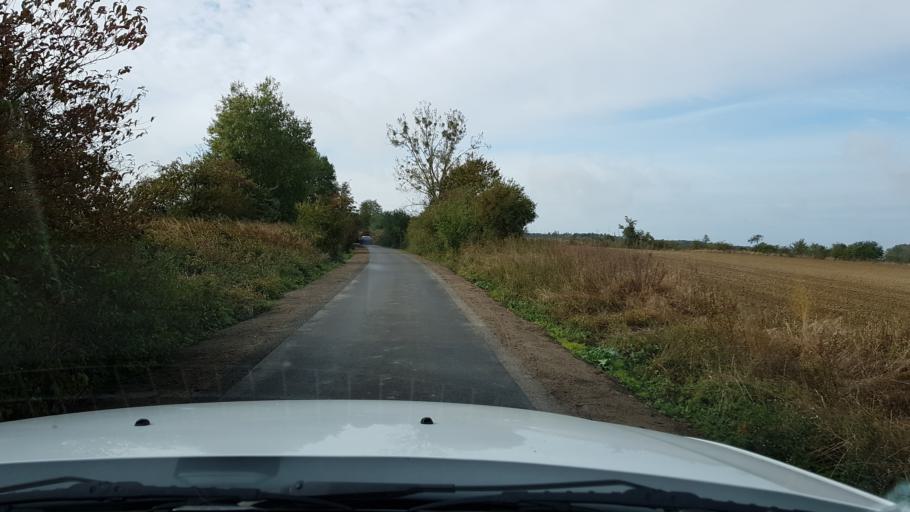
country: PL
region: West Pomeranian Voivodeship
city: Trzcinsko Zdroj
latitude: 52.9512
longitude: 14.5796
